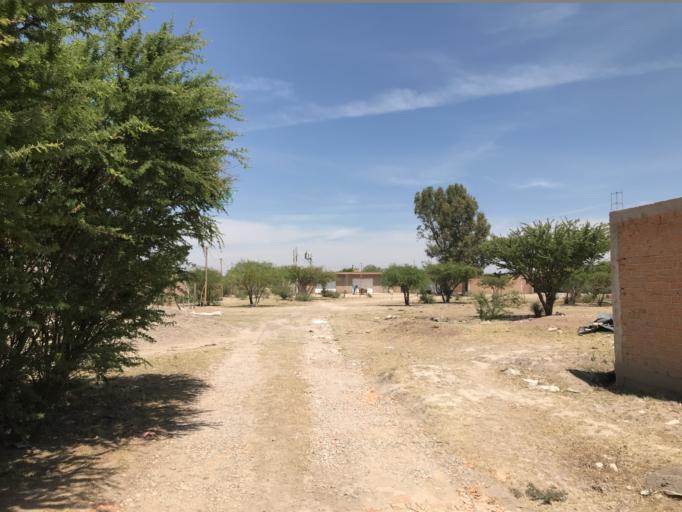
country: MX
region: Durango
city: Victoria de Durango
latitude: 23.9791
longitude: -104.6871
